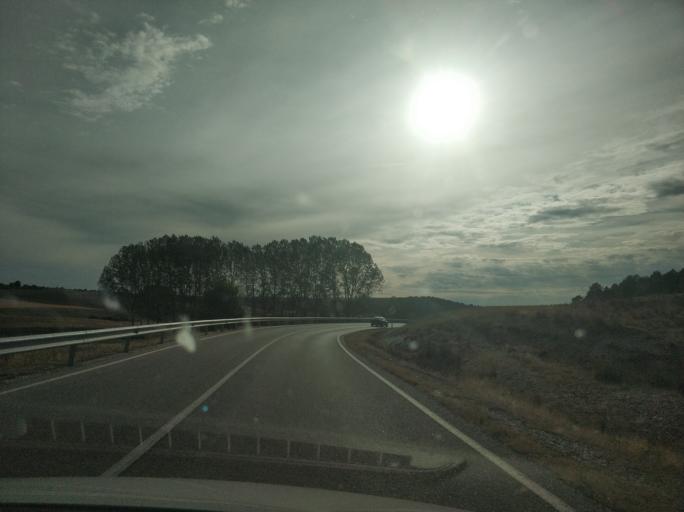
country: ES
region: Castille and Leon
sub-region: Provincia de Soria
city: Santa Maria de las Hoyas
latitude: 41.7692
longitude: -3.1471
